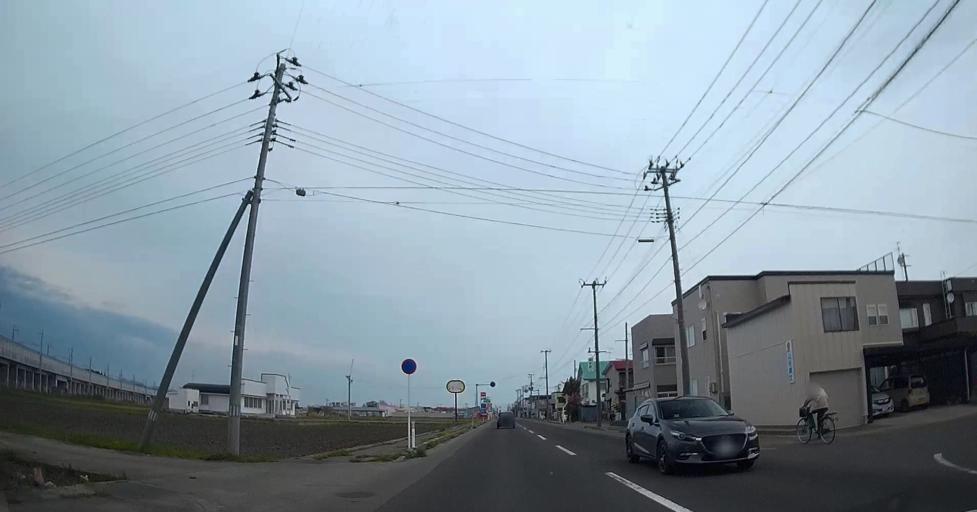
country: JP
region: Aomori
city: Aomori Shi
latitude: 40.8543
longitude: 140.6814
